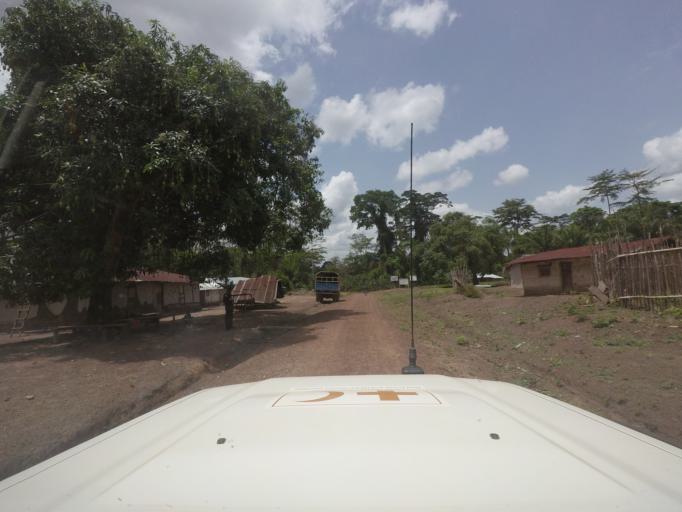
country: GN
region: Nzerekore
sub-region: Yomou
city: Yomou
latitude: 7.2820
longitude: -9.1831
